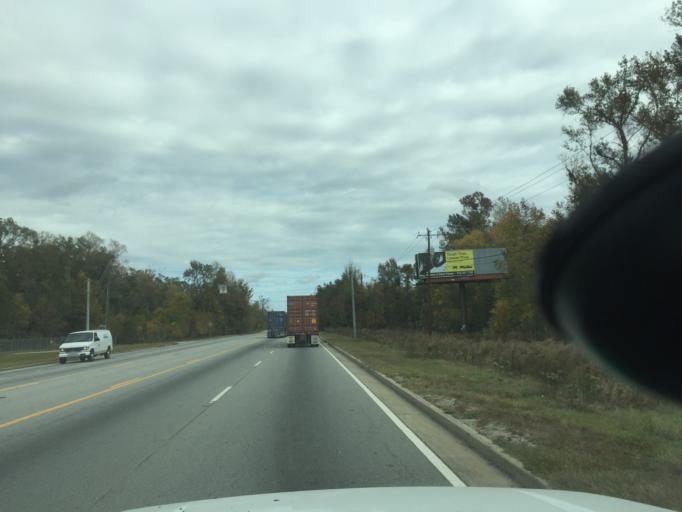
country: US
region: Georgia
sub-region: Chatham County
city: Garden City
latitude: 32.1211
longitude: -81.1876
